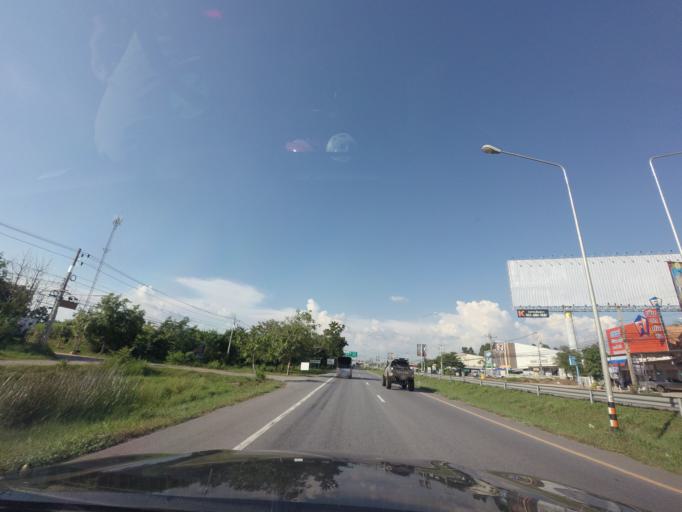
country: TH
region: Khon Kaen
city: Non Sila
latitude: 15.9628
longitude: 102.6902
